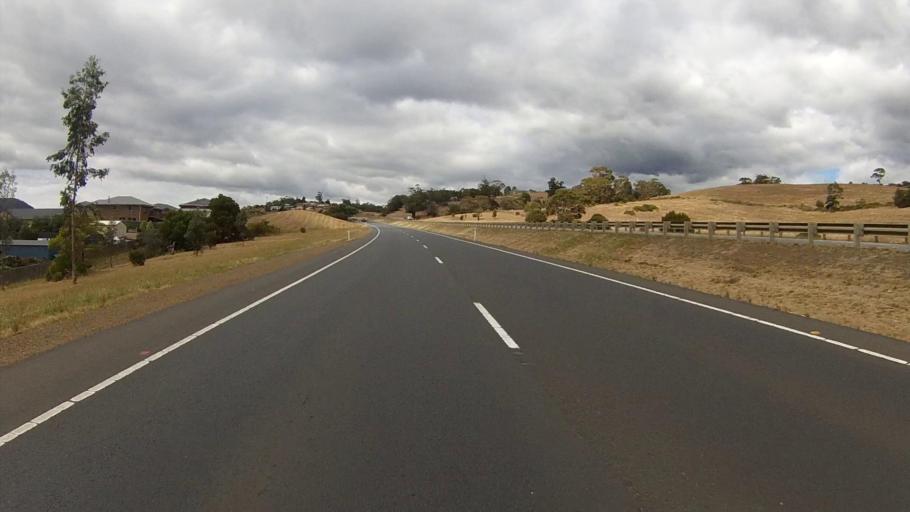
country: AU
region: Tasmania
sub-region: Glenorchy
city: Austins Ferry
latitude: -42.7671
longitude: 147.2360
